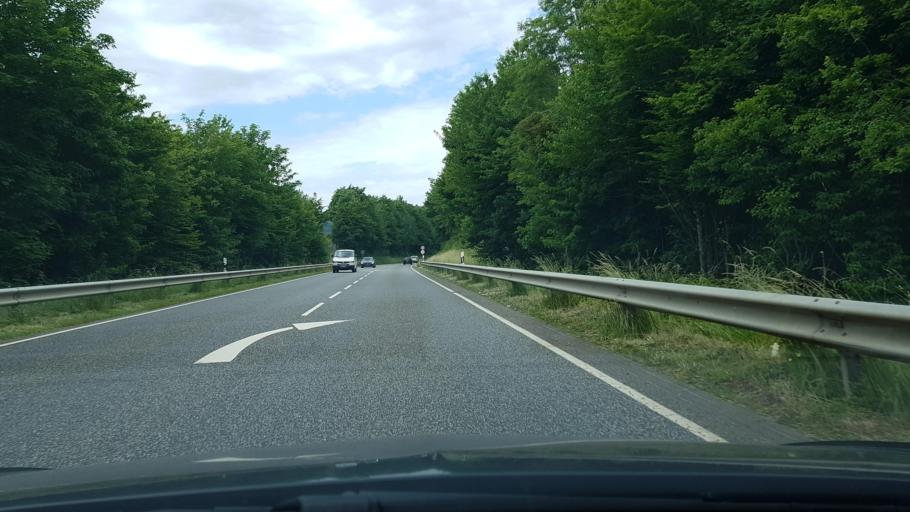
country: DE
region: Rheinland-Pfalz
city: Kempenich
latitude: 50.4181
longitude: 7.1319
